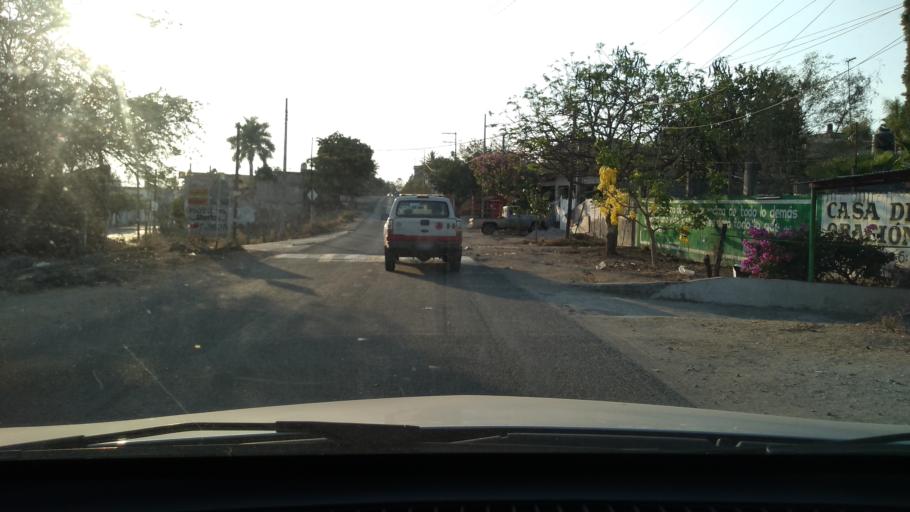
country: MX
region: Morelos
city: Puente de Ixtla
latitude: 18.6146
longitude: -99.3125
